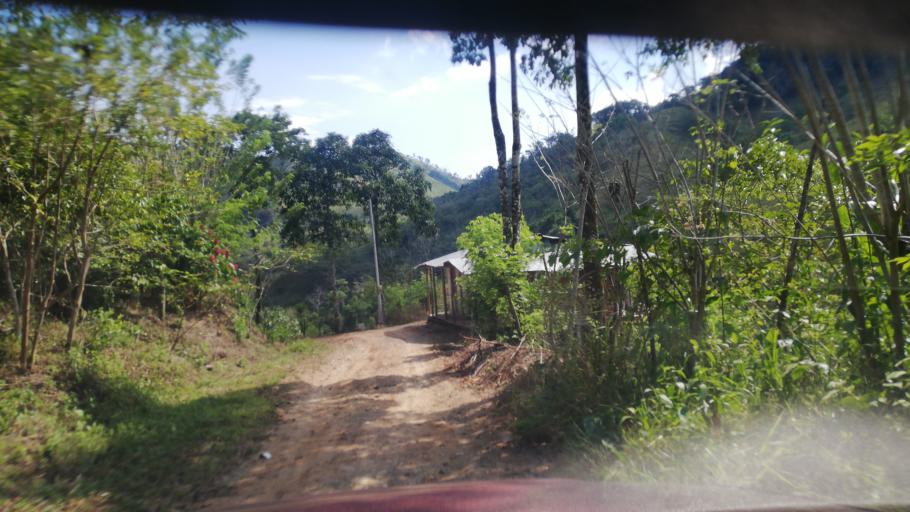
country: CO
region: Risaralda
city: Balboa
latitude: 4.9065
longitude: -75.9495
